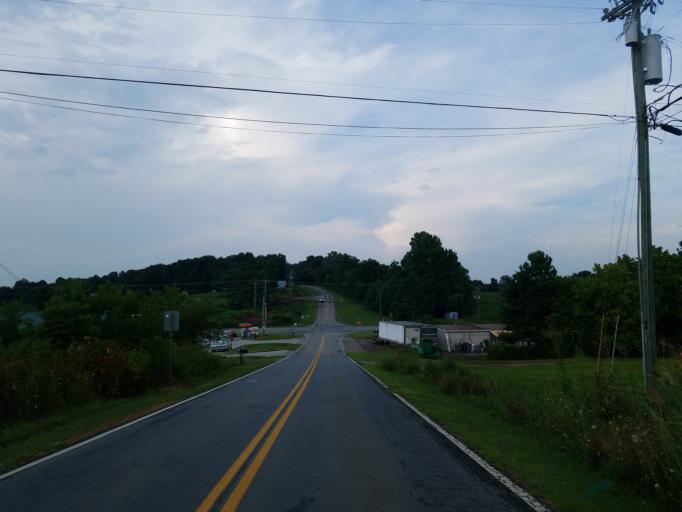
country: US
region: Georgia
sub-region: Pickens County
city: Jasper
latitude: 34.4688
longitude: -84.5096
